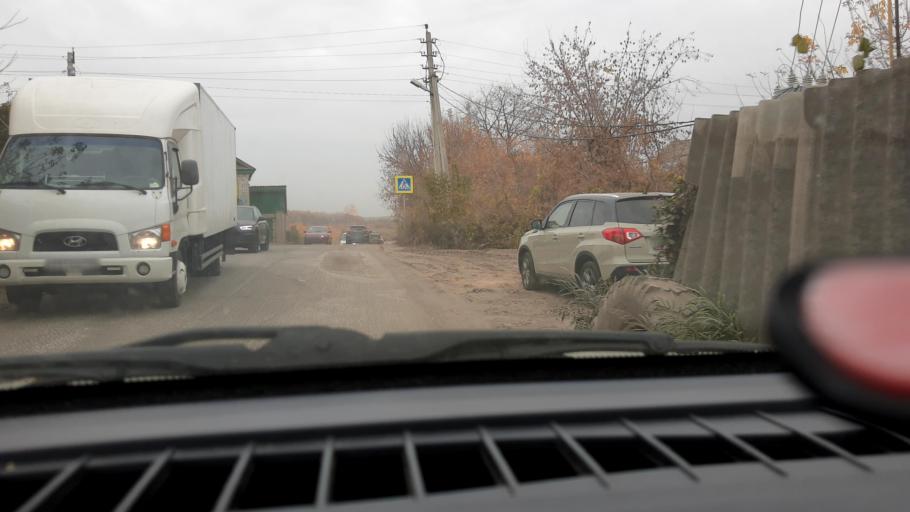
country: RU
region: Nizjnij Novgorod
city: Neklyudovo
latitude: 56.4119
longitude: 43.9761
